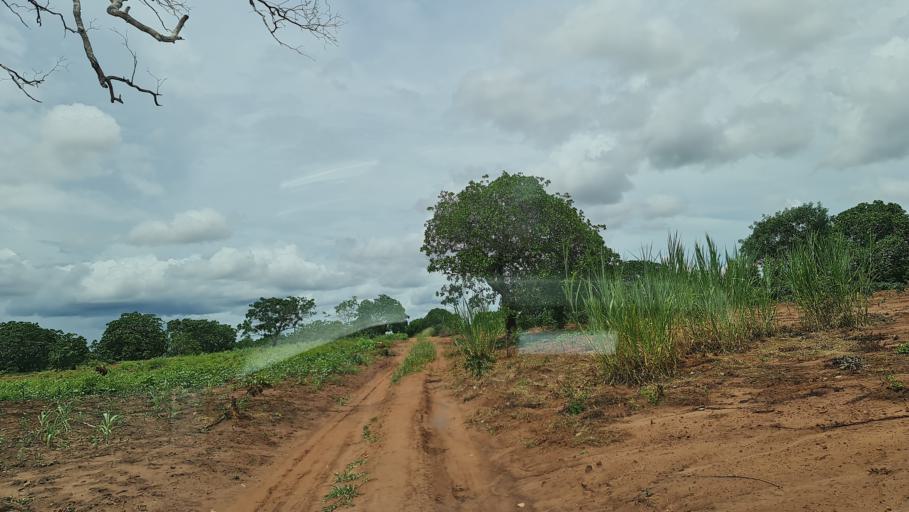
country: MZ
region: Nampula
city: Nacala
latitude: -14.7870
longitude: 39.9759
